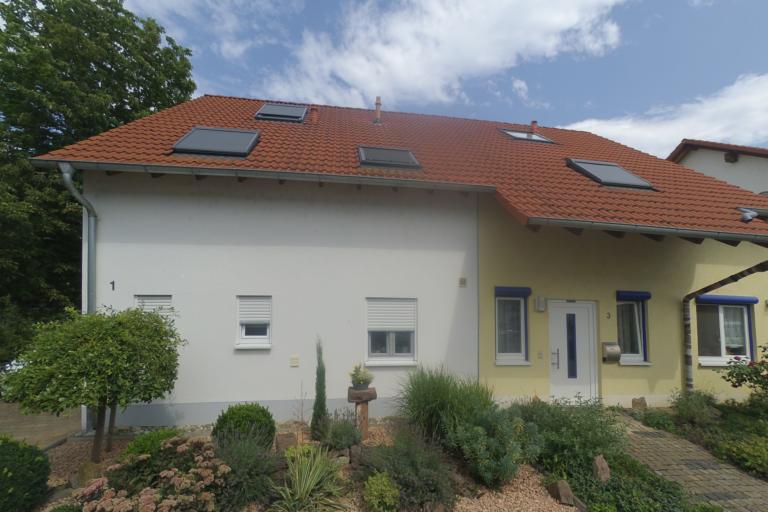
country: DE
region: Rheinland-Pfalz
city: Frankenthal
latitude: 49.5155
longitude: 8.3365
